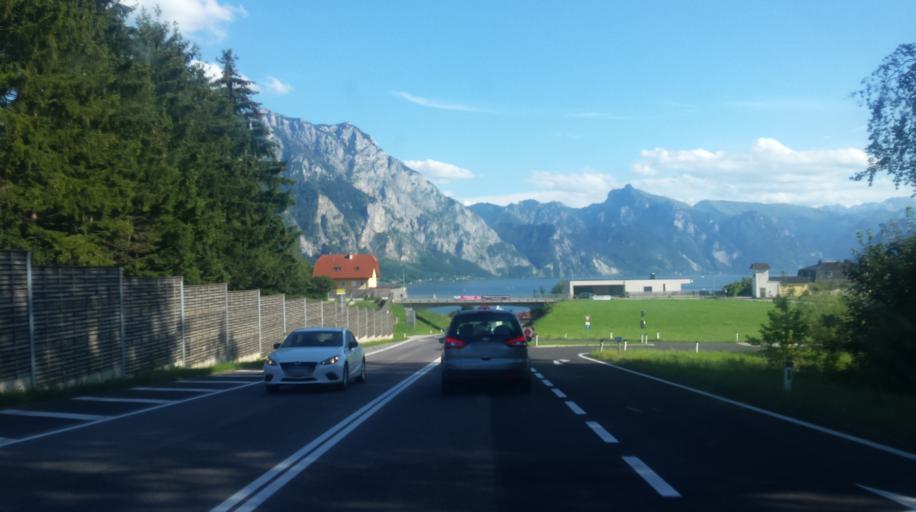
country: AT
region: Upper Austria
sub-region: Politischer Bezirk Gmunden
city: Altmunster
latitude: 47.9123
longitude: 13.7784
